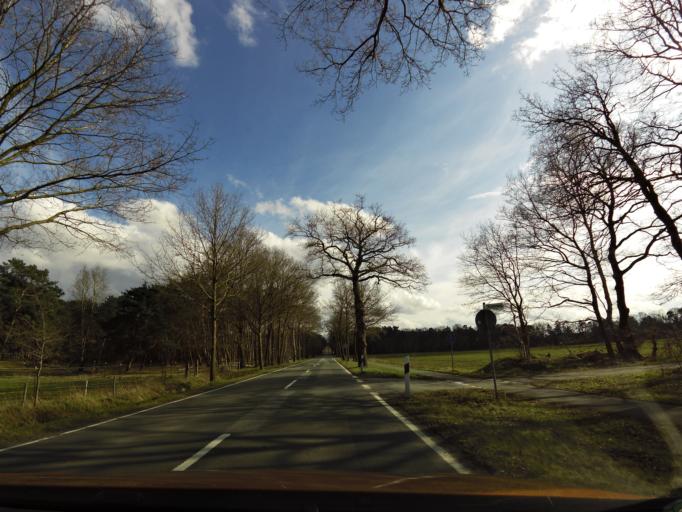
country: DE
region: Lower Saxony
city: Hatten
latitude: 53.0293
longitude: 8.3410
